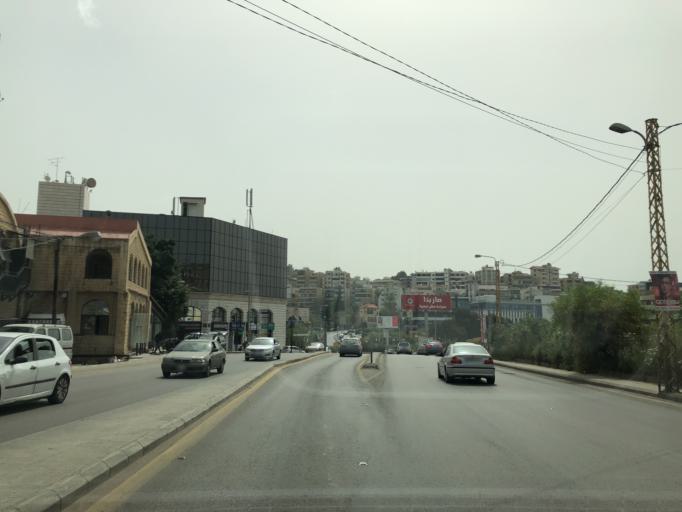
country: LB
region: Mont-Liban
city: Baabda
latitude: 33.8632
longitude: 35.5400
